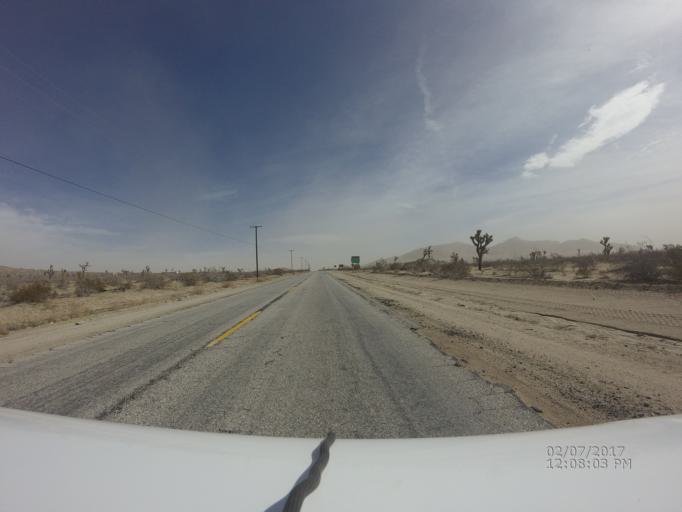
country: US
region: California
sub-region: Los Angeles County
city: Lake Los Angeles
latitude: 34.6898
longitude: -117.8300
